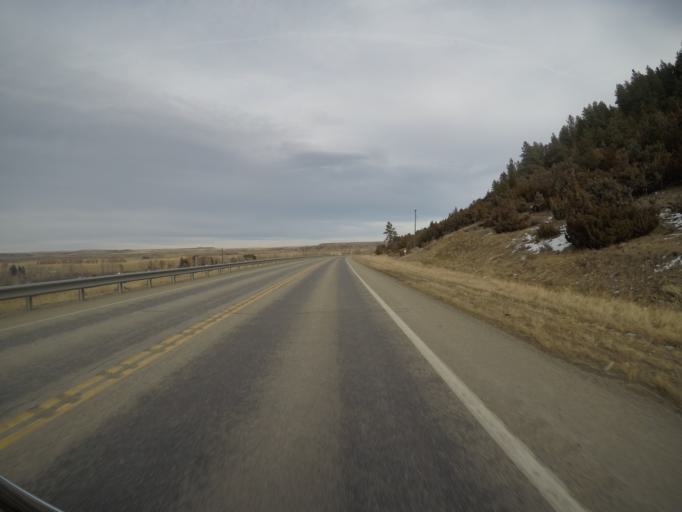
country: US
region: Montana
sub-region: Stillwater County
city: Absarokee
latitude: 45.5308
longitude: -109.4280
